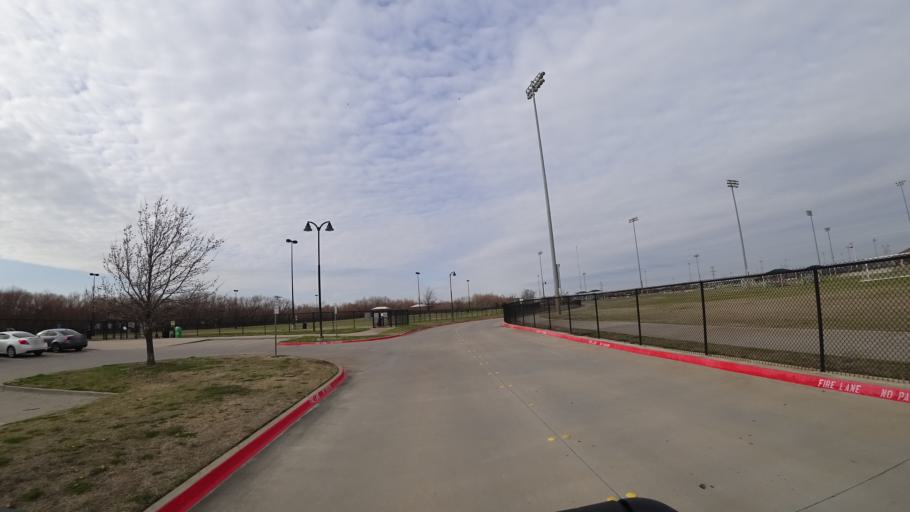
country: US
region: Texas
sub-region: Denton County
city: Lewisville
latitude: 33.0305
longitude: -96.9725
